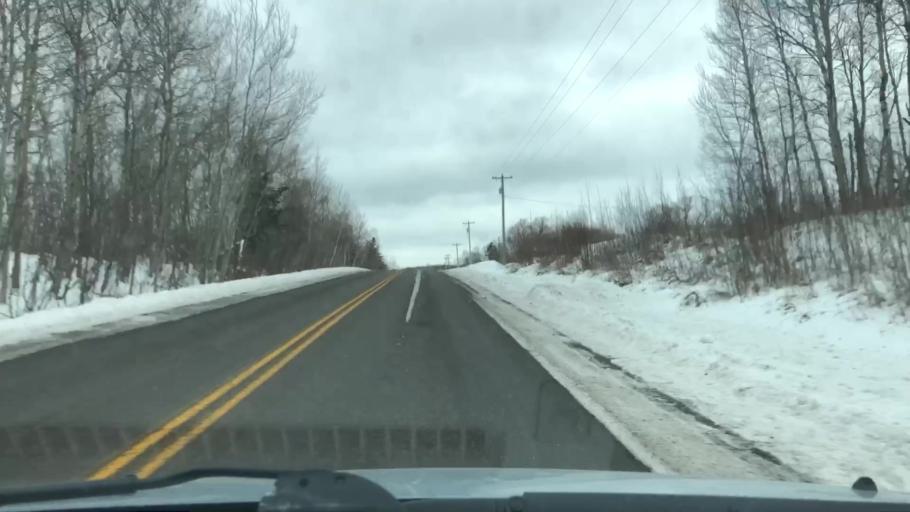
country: US
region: Minnesota
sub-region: Saint Louis County
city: Proctor
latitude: 46.7022
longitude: -92.2869
